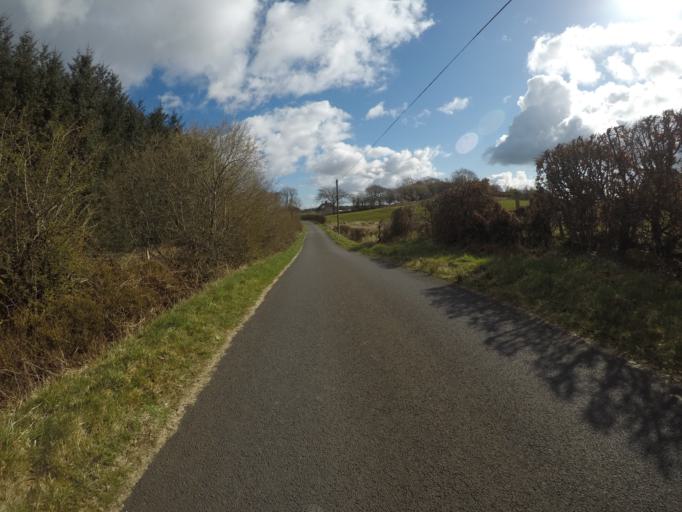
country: GB
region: Scotland
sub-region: North Ayrshire
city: Beith
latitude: 55.7082
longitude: -4.6592
